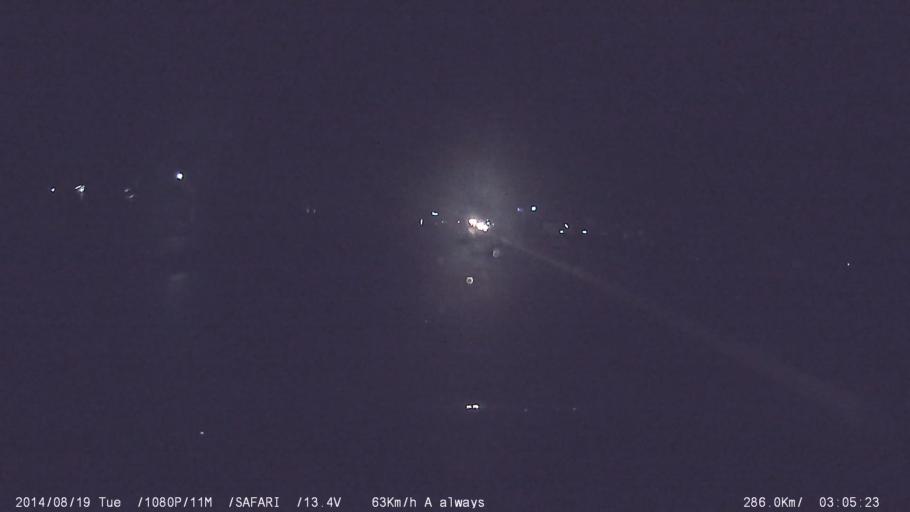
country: IN
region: Tamil Nadu
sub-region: Coimbatore
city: Sulur
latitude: 11.0782
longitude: 77.1160
